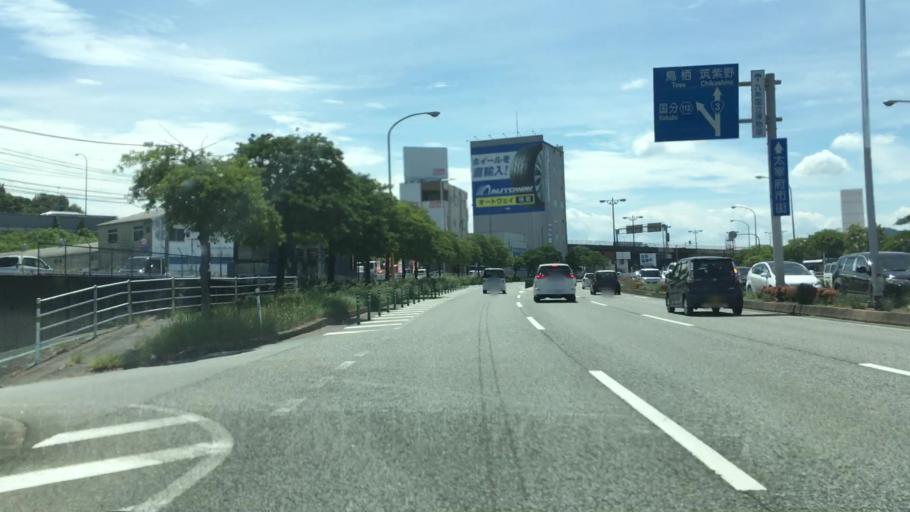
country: JP
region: Fukuoka
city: Onojo
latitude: 33.5281
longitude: 130.4945
